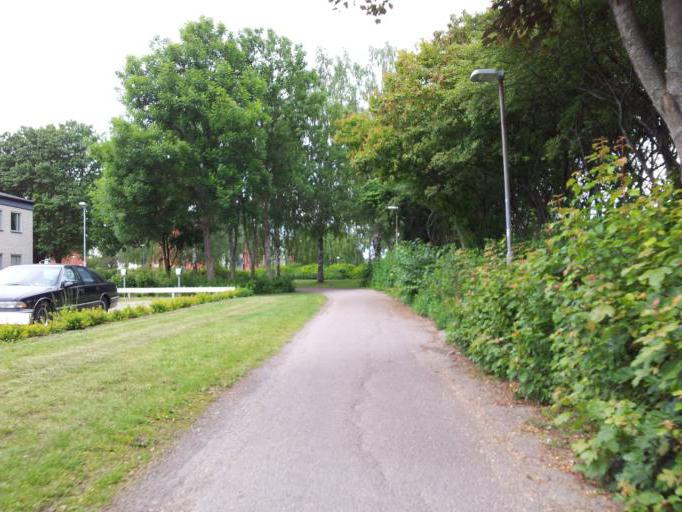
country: SE
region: Uppsala
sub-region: Uppsala Kommun
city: Uppsala
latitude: 59.8728
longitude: 17.6486
